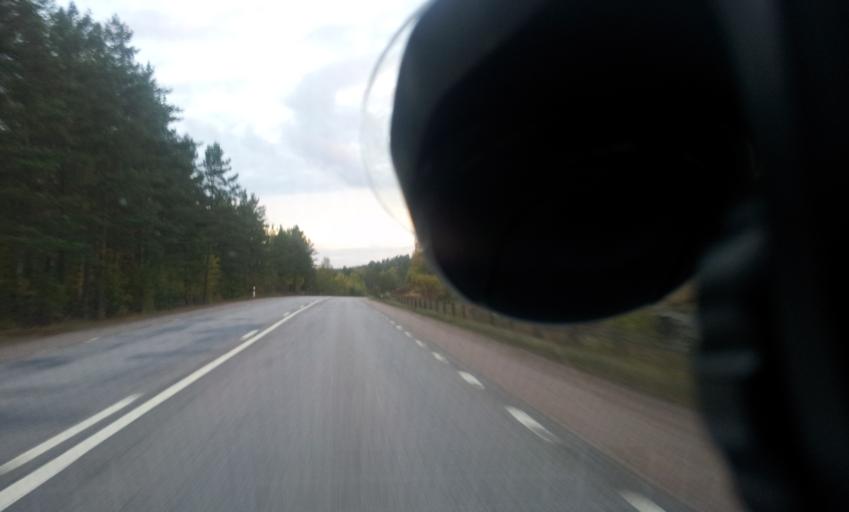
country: SE
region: Kalmar
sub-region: Vasterviks Kommun
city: Ankarsrum
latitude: 57.6385
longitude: 16.4483
